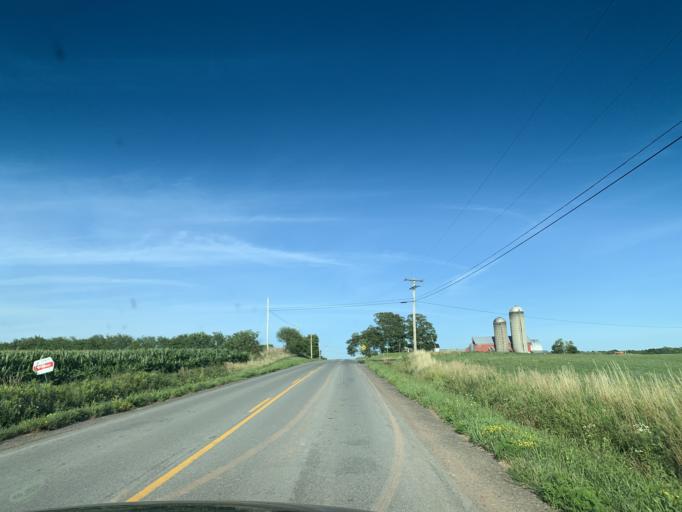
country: US
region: New York
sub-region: Oneida County
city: Vernon
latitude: 43.0558
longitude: -75.4796
